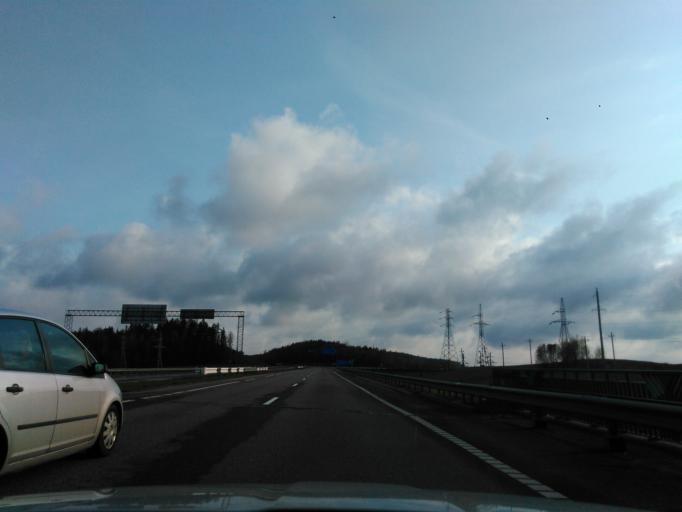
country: BY
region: Minsk
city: Lahoysk
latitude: 54.2073
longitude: 27.8217
